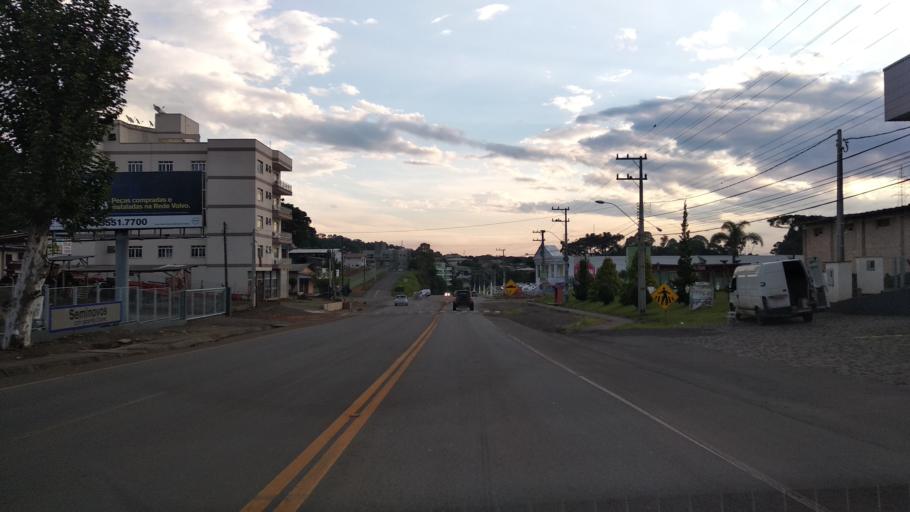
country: BR
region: Santa Catarina
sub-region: Videira
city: Videira
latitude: -26.9995
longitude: -51.1199
